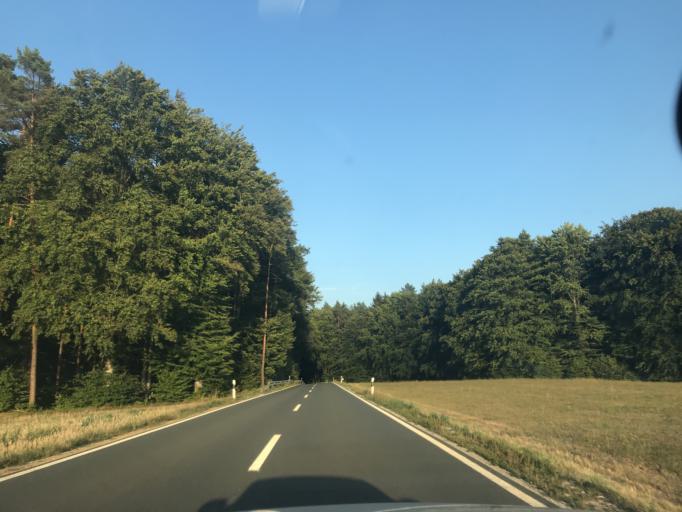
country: DE
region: Bavaria
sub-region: Upper Franconia
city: Pottenstein
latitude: 49.7122
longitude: 11.4221
